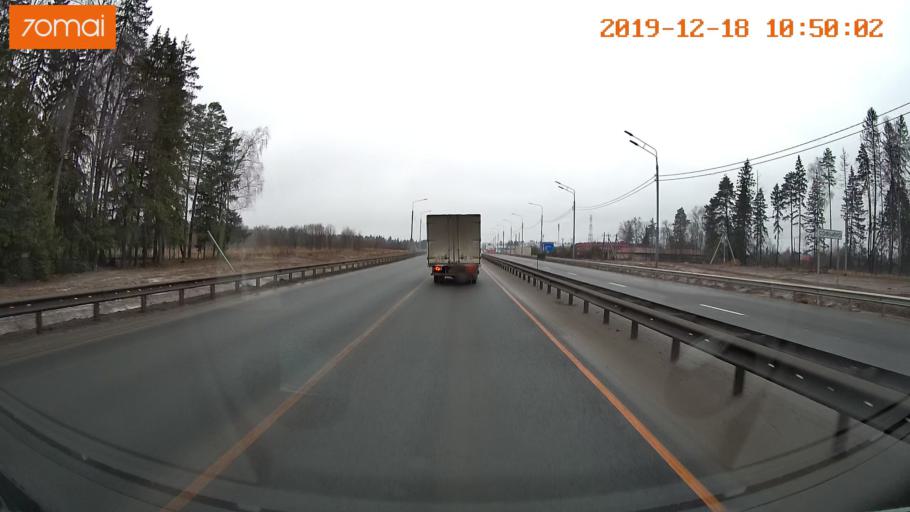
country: RU
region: Moskovskaya
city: Selyatino
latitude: 55.5067
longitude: 37.0110
